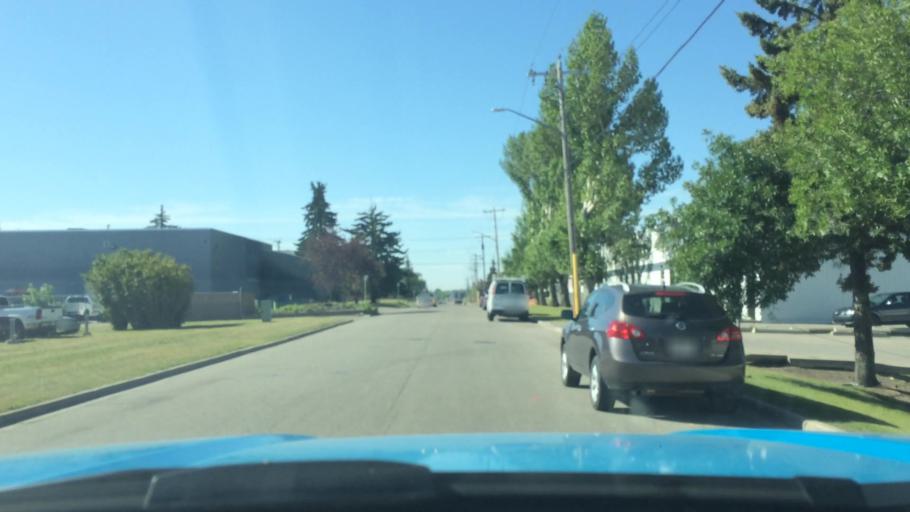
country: CA
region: Alberta
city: Calgary
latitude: 51.0894
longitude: -114.0051
